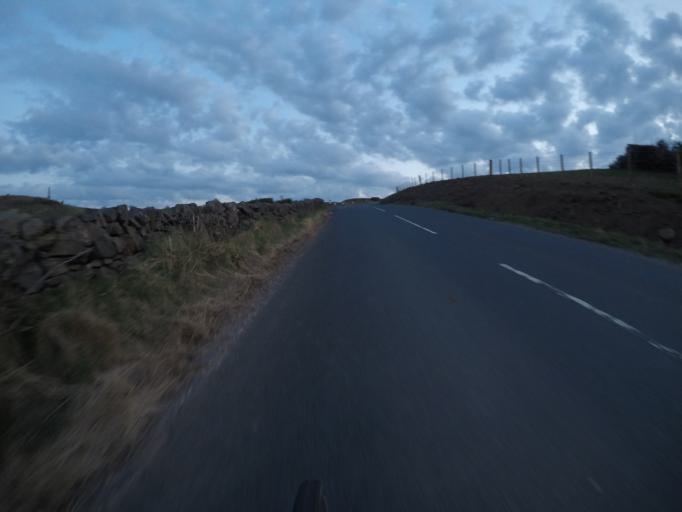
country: GB
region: Scotland
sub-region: South Ayrshire
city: Dundonald
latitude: 55.5631
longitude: -4.6048
